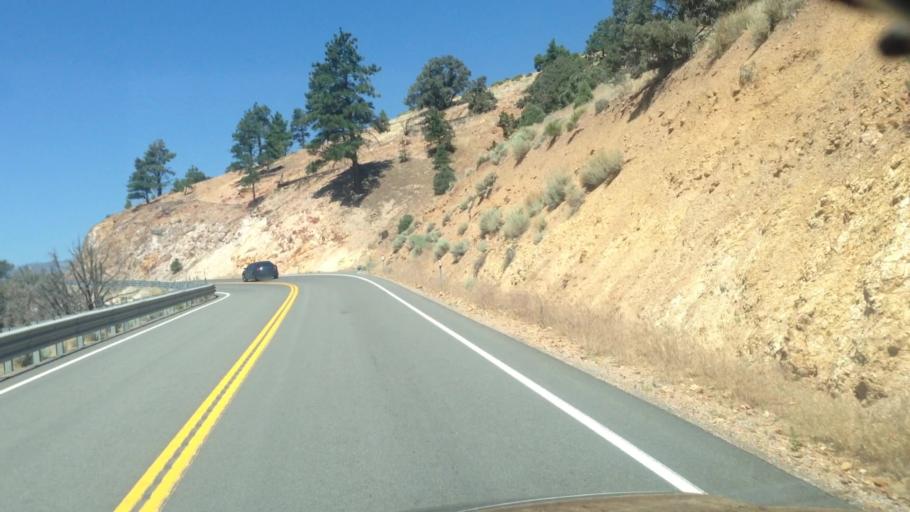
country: US
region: Nevada
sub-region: Storey County
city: Virginia City
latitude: 39.3897
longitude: -119.7071
